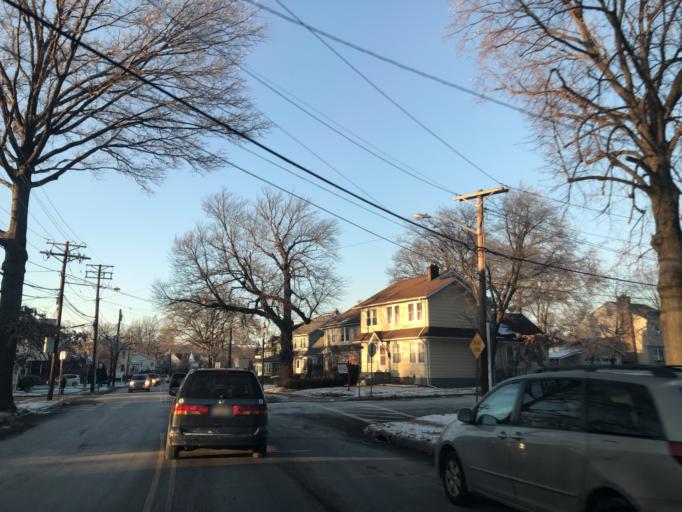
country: US
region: New Jersey
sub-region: Essex County
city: South Orange
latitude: 40.7376
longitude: -74.2514
